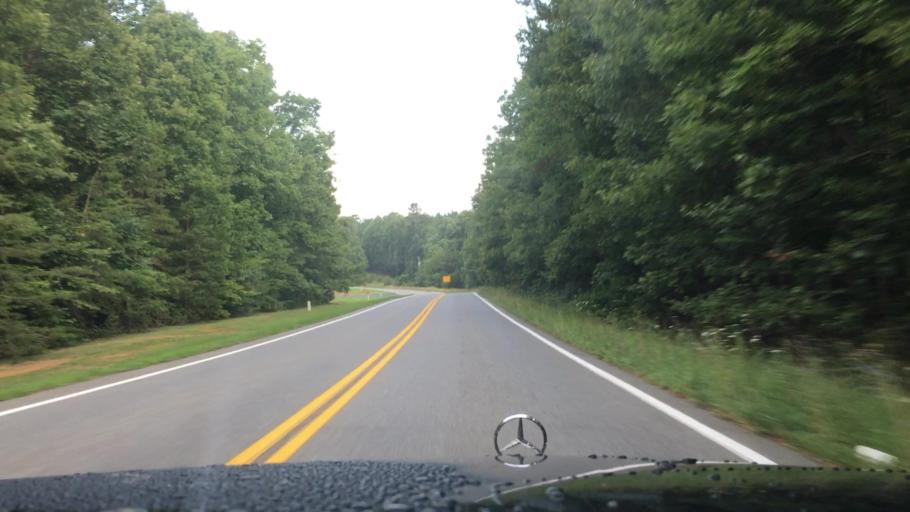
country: US
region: Virginia
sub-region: Campbell County
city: Altavista
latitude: 37.1464
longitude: -79.2716
